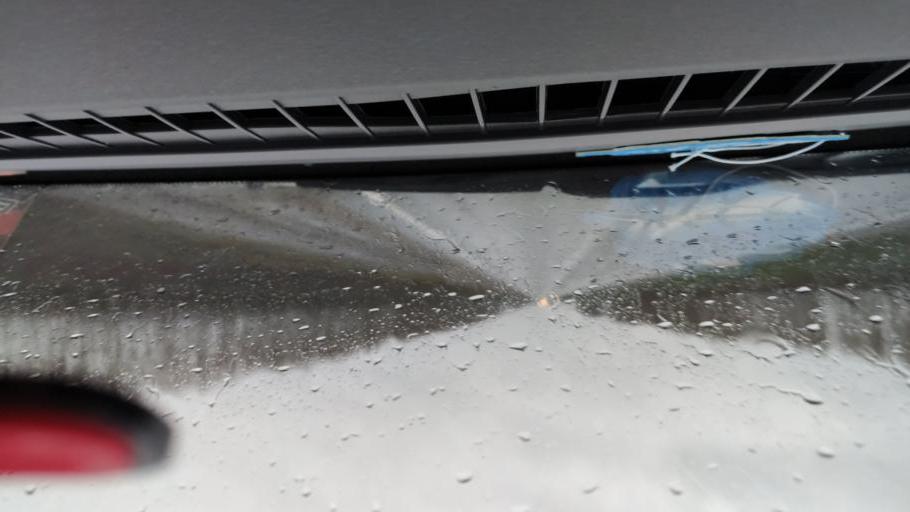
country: RU
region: Tatarstan
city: Mendeleyevsk
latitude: 55.9301
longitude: 52.2813
